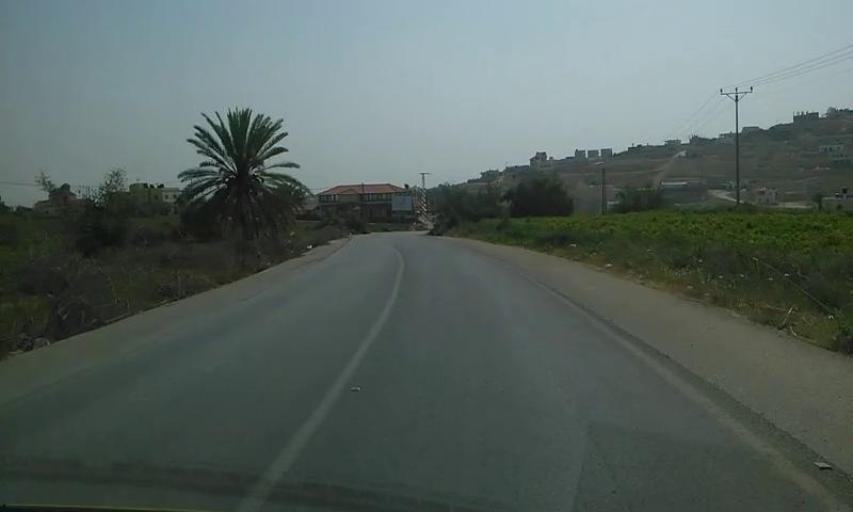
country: PS
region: West Bank
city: An Nuway`imah
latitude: 31.8835
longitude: 35.4372
